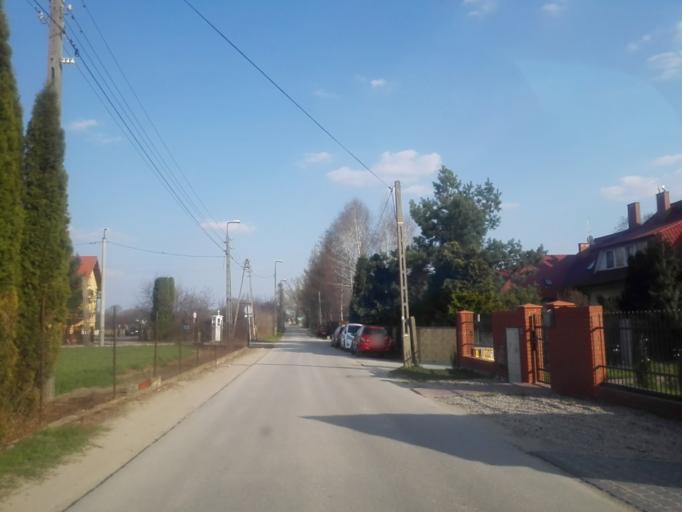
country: PL
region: Masovian Voivodeship
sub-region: Powiat piaseczynski
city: Konstancin-Jeziorna
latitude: 52.1386
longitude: 21.1453
